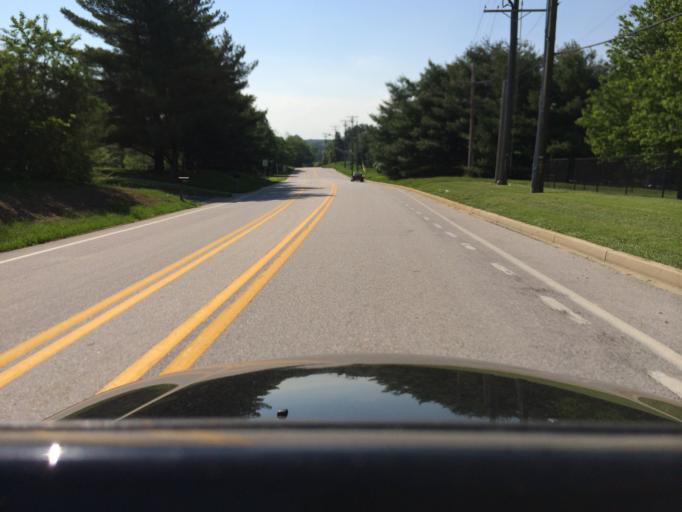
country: US
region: Maryland
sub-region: Howard County
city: Highland
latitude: 39.1906
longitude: -76.9278
